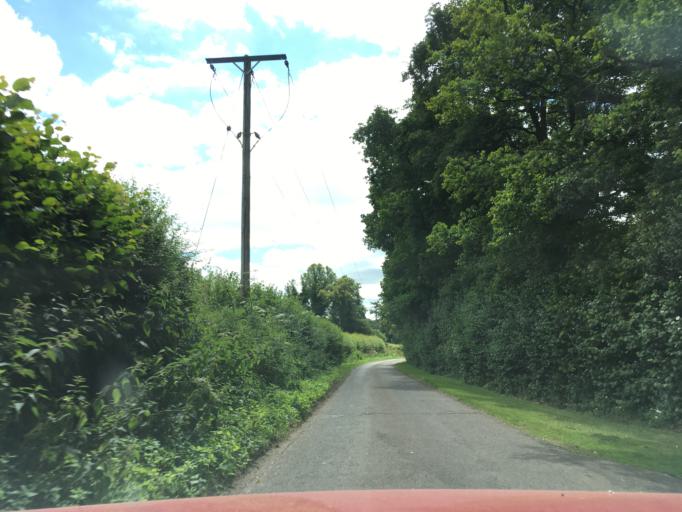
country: GB
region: England
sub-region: Hampshire
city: Highclere
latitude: 51.2861
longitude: -1.4170
